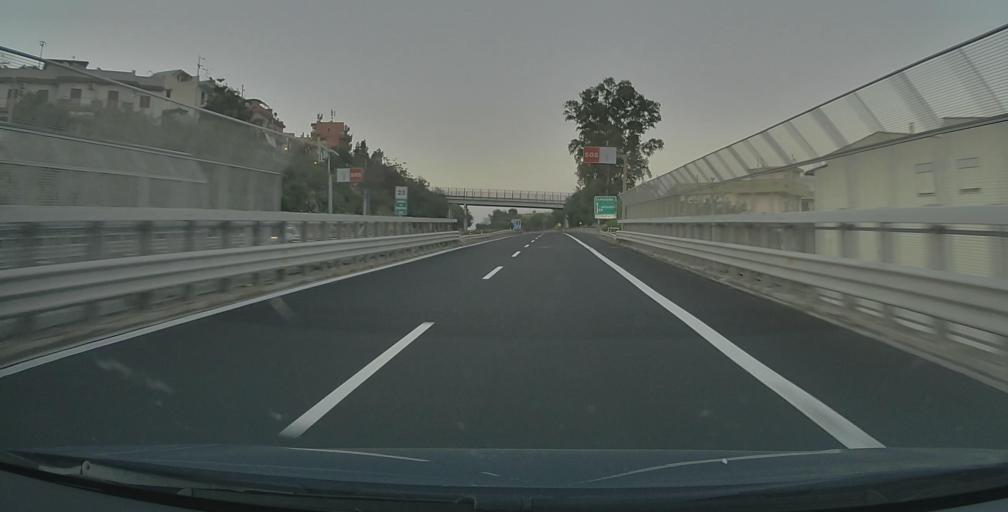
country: IT
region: Sicily
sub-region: Messina
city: Furci Siculo
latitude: 37.9624
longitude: 15.3783
